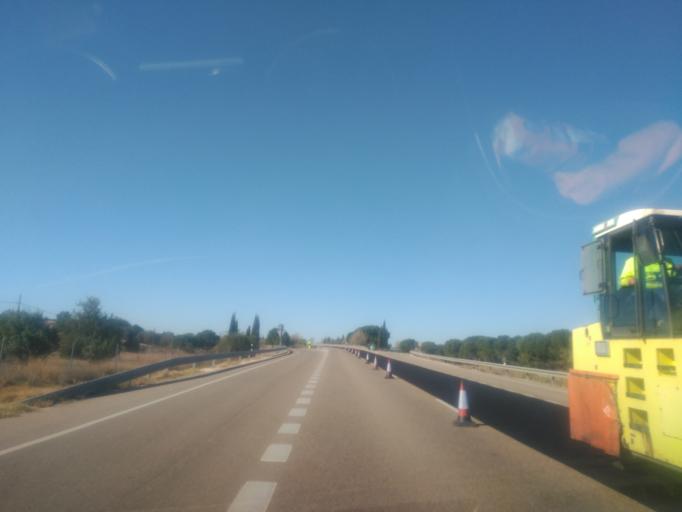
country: ES
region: Castille and Leon
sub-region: Provincia de Valladolid
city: Quintanilla de Onesimo
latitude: 41.6270
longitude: -4.3448
